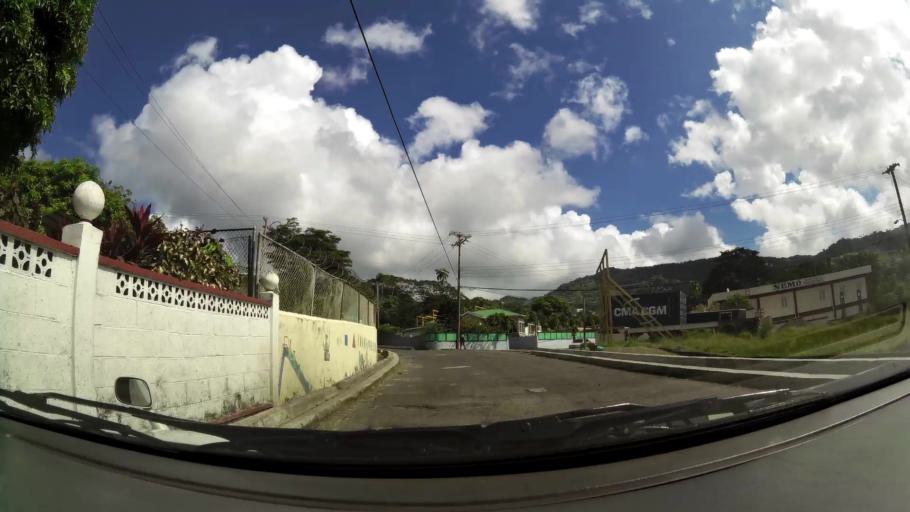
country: VC
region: Saint George
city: Kingstown
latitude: 13.1623
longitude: -61.2289
